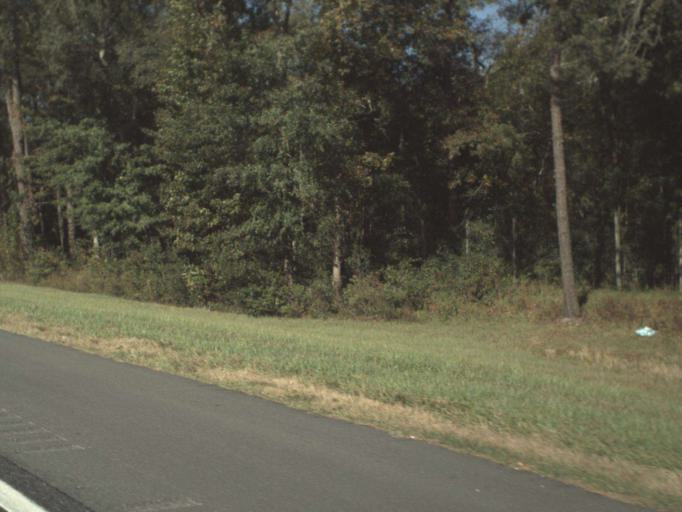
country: US
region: Florida
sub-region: Jefferson County
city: Monticello
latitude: 30.4803
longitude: -84.0562
